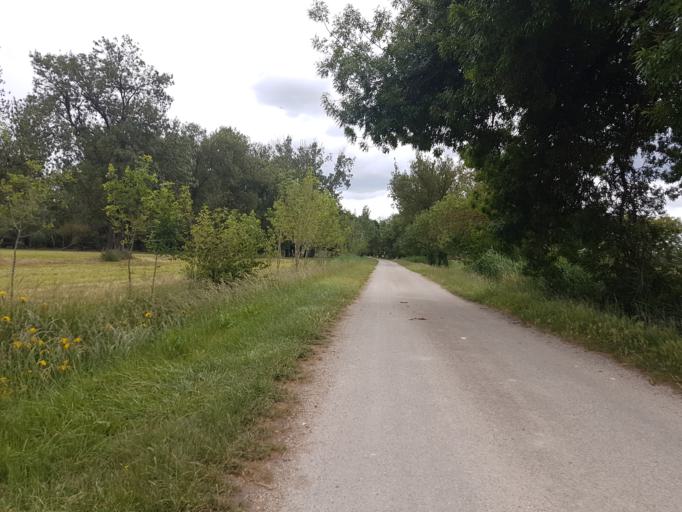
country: FR
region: Languedoc-Roussillon
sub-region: Departement du Gard
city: Fourques
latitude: 43.7096
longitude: 4.5735
